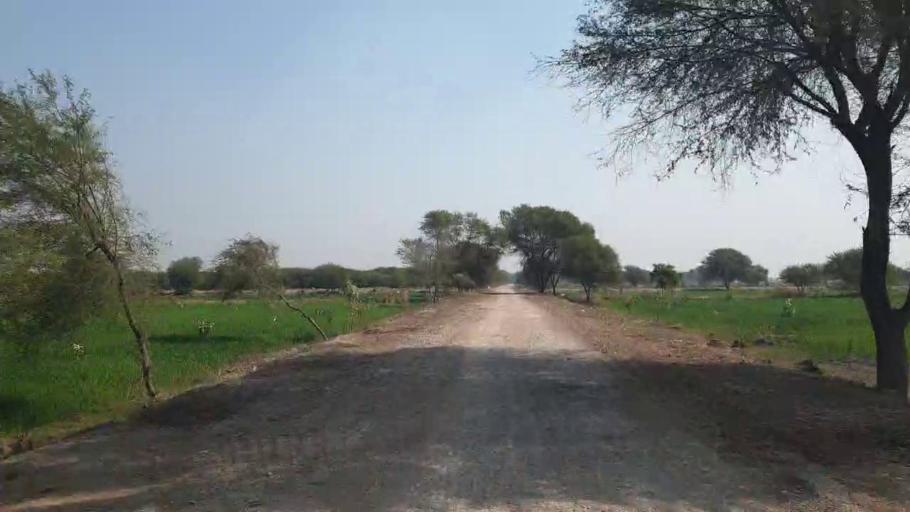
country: PK
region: Sindh
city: Chambar
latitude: 25.3521
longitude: 68.9258
